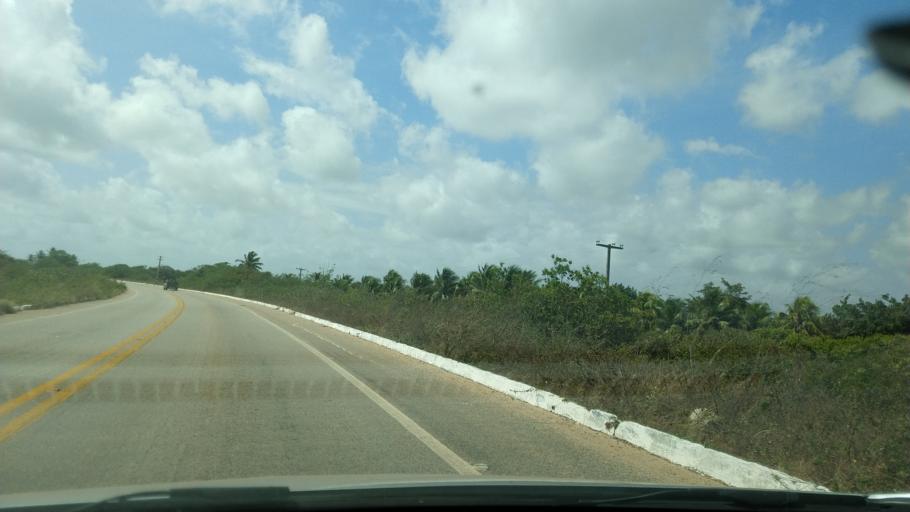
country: BR
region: Rio Grande do Norte
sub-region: Touros
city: Touros
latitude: -5.1851
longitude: -35.5117
